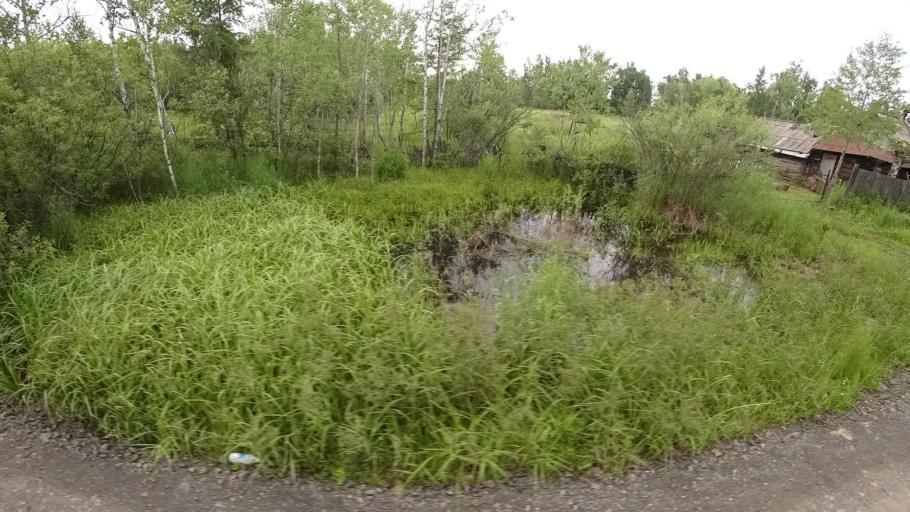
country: RU
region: Khabarovsk Krai
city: Amursk
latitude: 49.8977
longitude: 136.1301
